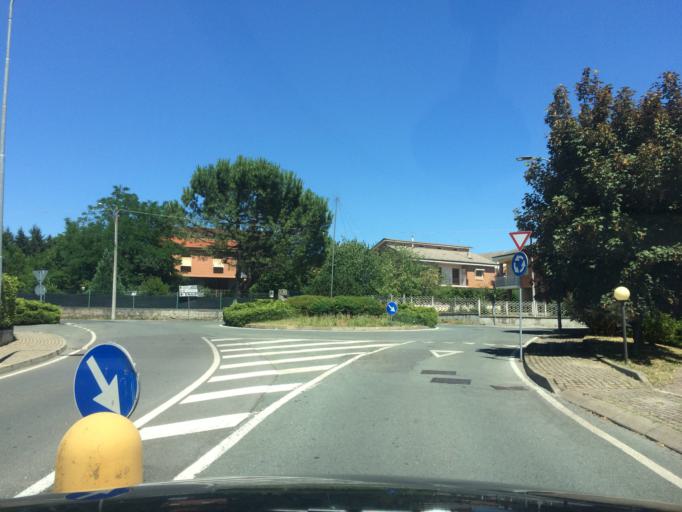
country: IT
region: Piedmont
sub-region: Provincia di Alessandria
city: Acqui Terme
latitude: 44.6808
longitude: 8.4608
